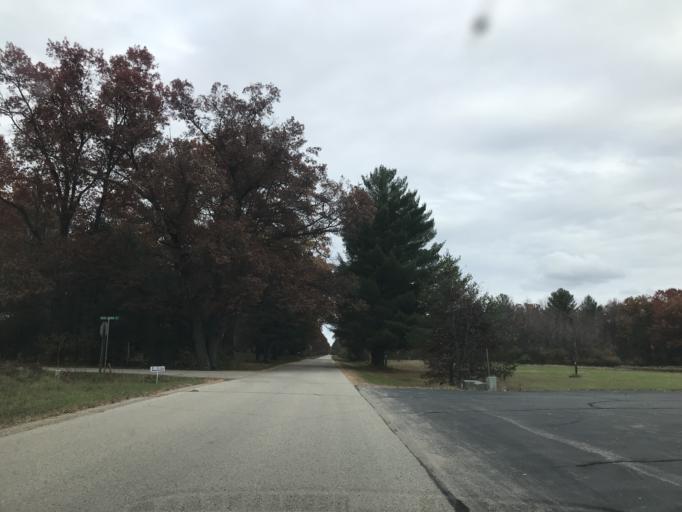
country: US
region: Wisconsin
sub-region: Marinette County
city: Peshtigo
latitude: 45.0711
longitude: -87.7390
